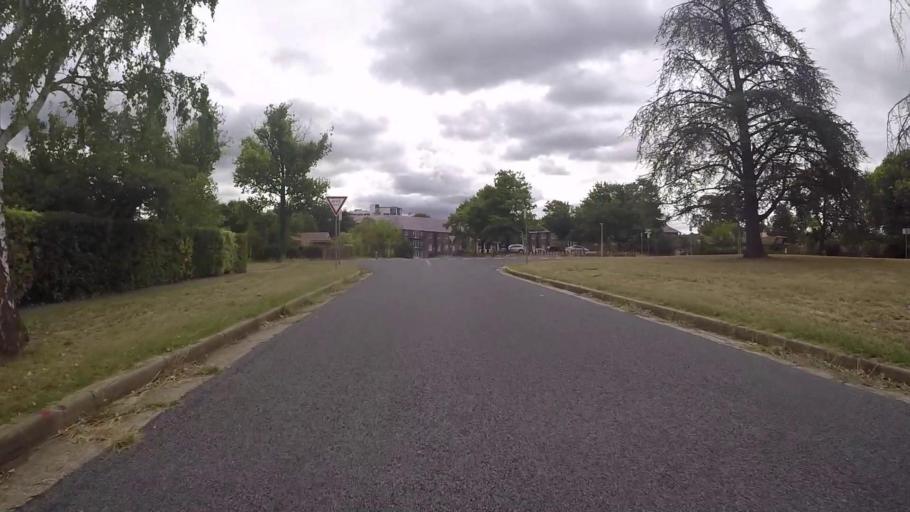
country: AU
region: Australian Capital Territory
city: Forrest
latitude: -35.3121
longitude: 149.1369
